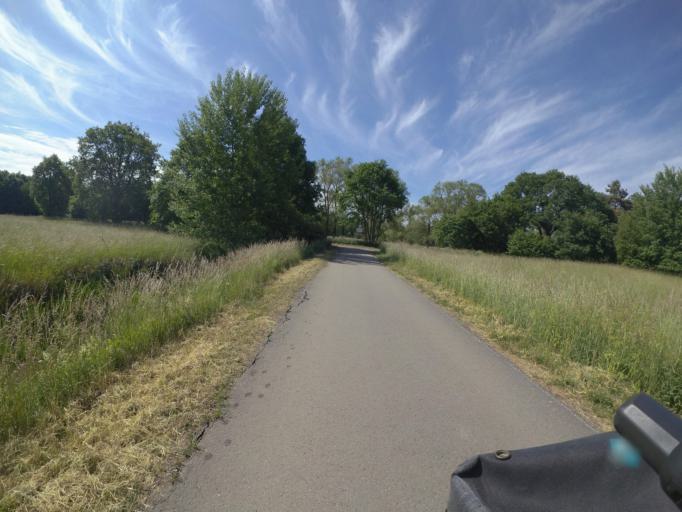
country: DE
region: Rheinland-Pfalz
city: Landstuhl
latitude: 49.4300
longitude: 7.5672
